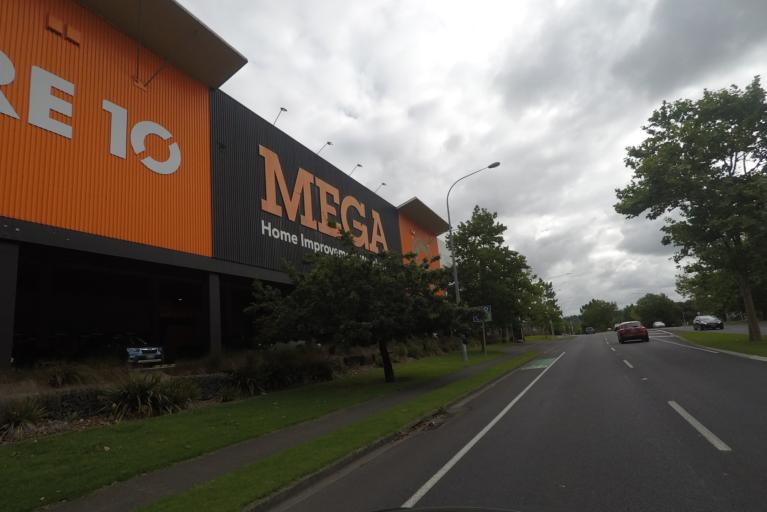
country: NZ
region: Auckland
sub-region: Auckland
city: Rothesay Bay
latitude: -36.7217
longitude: 174.7064
